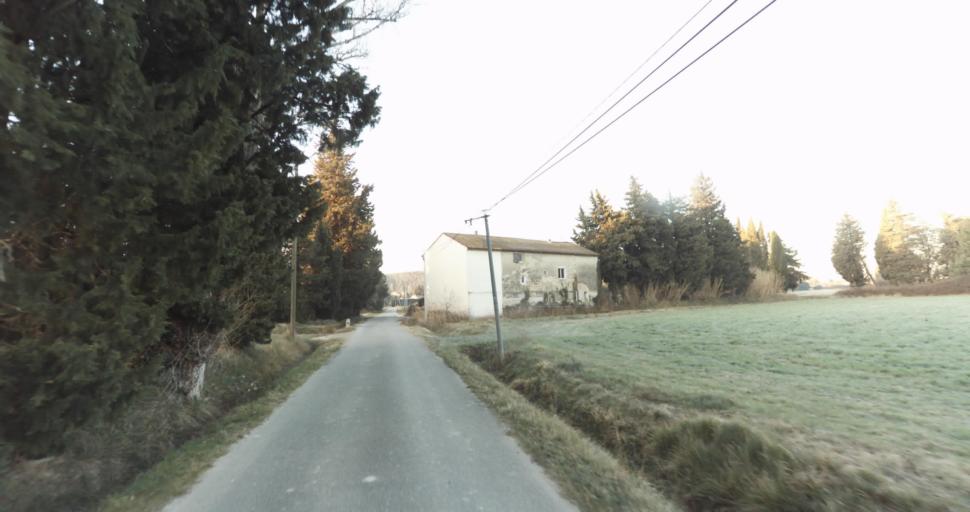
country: FR
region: Provence-Alpes-Cote d'Azur
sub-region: Departement des Bouches-du-Rhone
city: Barbentane
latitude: 43.9033
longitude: 4.7715
